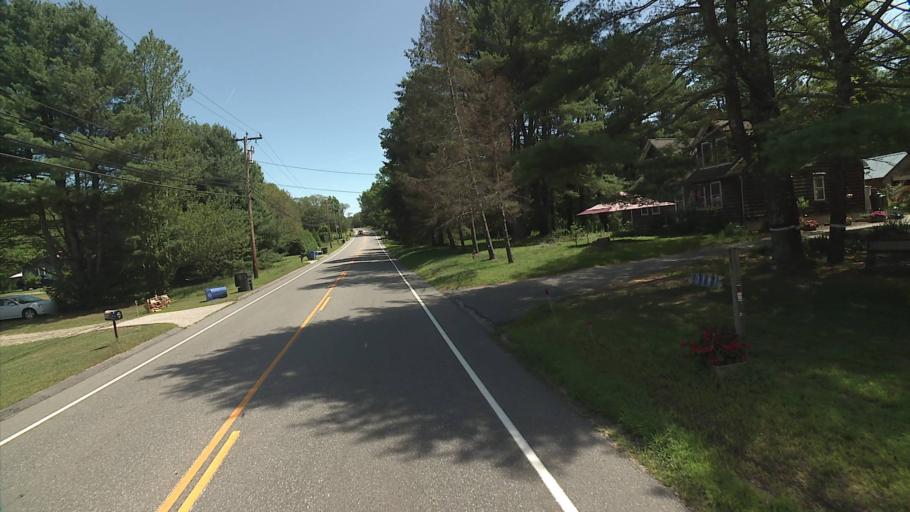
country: US
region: Connecticut
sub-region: Windham County
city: Killingly Center
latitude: 41.8446
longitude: -71.8346
